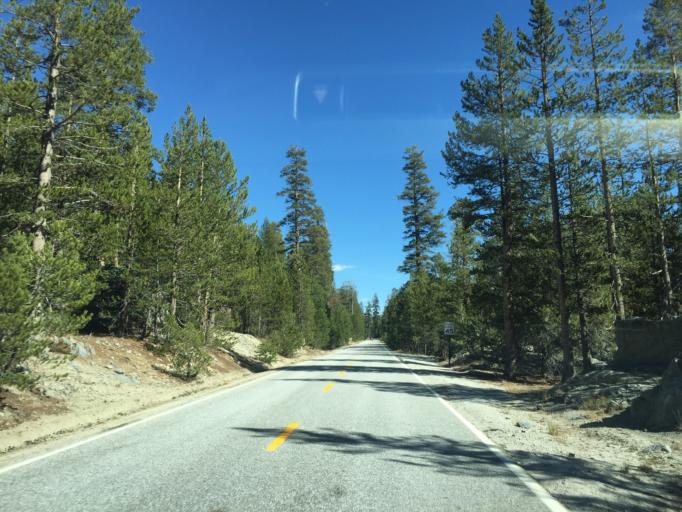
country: US
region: California
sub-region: Mariposa County
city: Yosemite Valley
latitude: 37.8067
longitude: -119.5615
